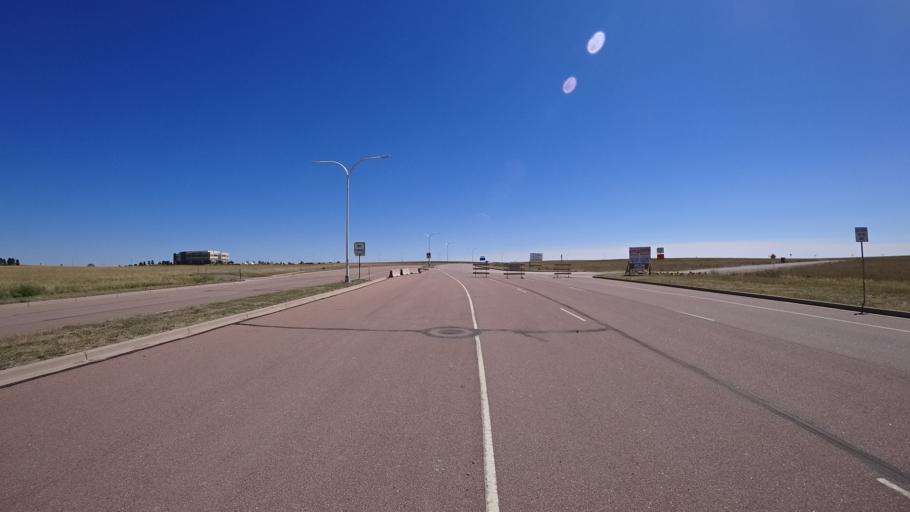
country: US
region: Colorado
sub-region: El Paso County
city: Security-Widefield
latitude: 38.7771
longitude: -104.7075
